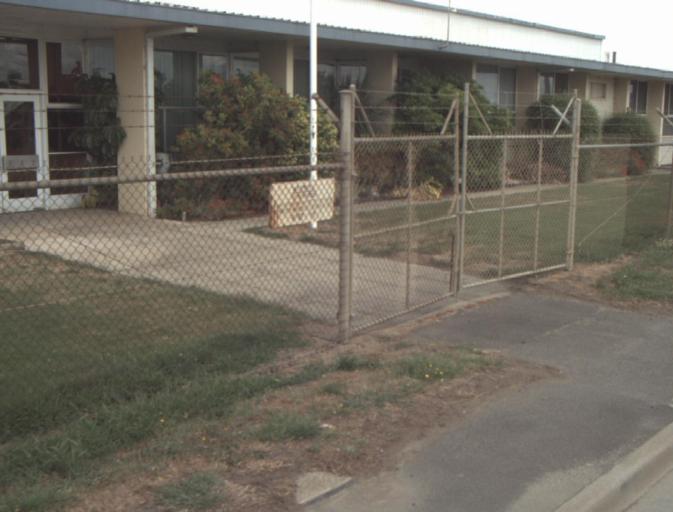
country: AU
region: Tasmania
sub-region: Launceston
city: Newnham
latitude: -41.4058
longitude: 147.1456
